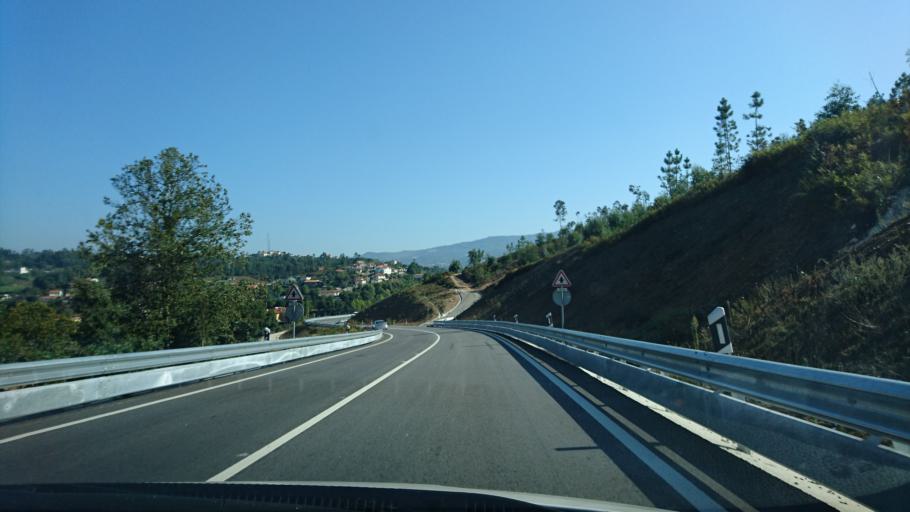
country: PT
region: Vila Real
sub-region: Mondim de Basto
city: Mondim de Basto
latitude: 41.4087
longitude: -7.9804
